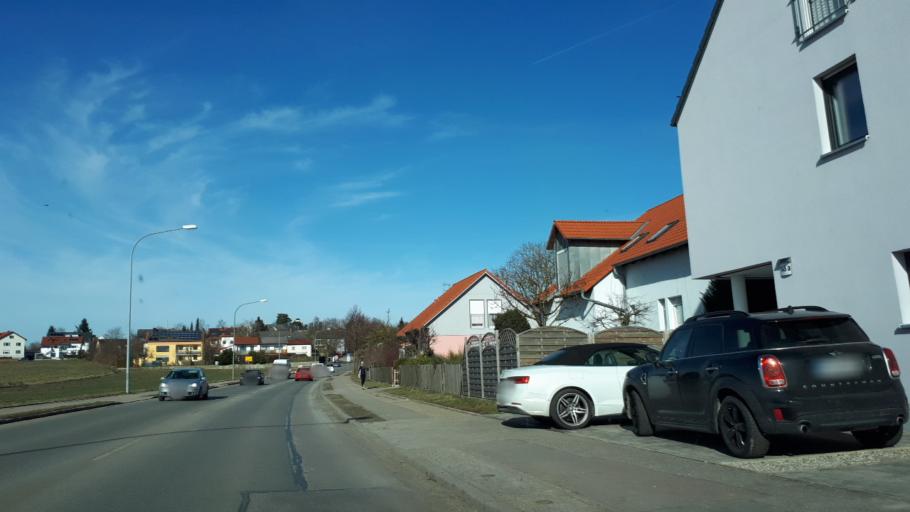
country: DE
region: Bavaria
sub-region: Upper Palatinate
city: Pentling
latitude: 48.9850
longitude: 12.0654
